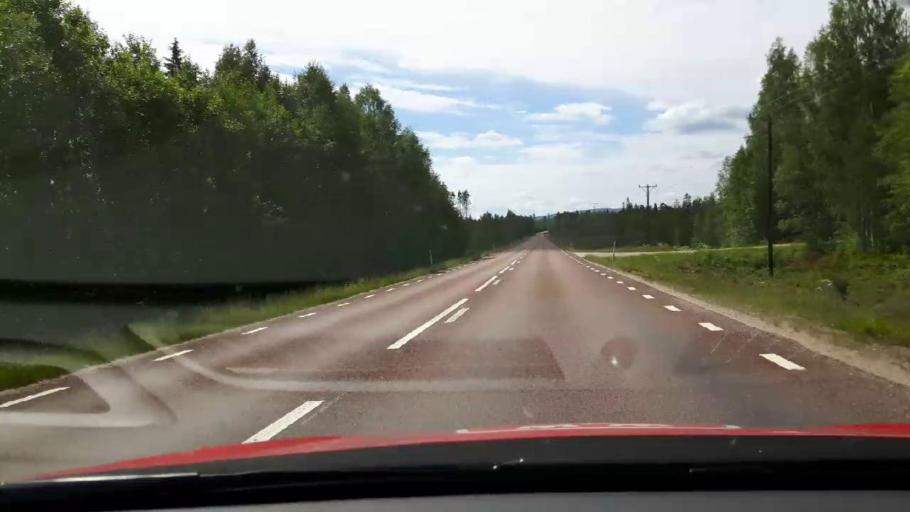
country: SE
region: Jaemtland
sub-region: Harjedalens Kommun
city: Sveg
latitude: 62.0594
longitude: 14.9105
